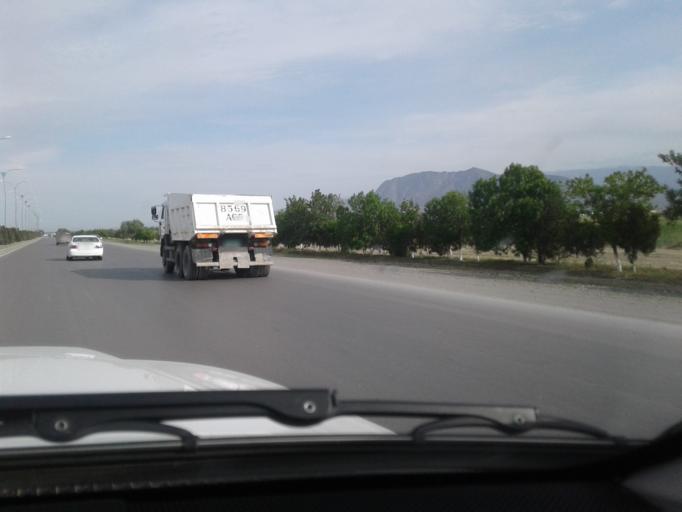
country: TM
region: Ahal
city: Abadan
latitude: 38.1410
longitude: 57.9990
